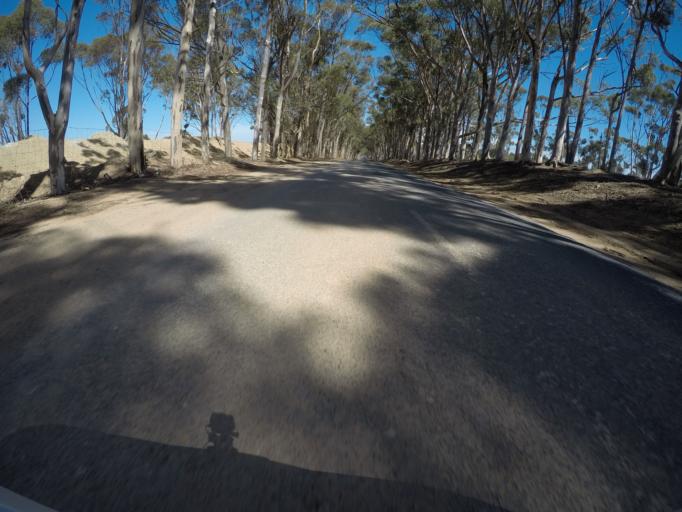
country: ZA
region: Western Cape
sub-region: City of Cape Town
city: Sunset Beach
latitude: -33.7596
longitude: 18.5535
